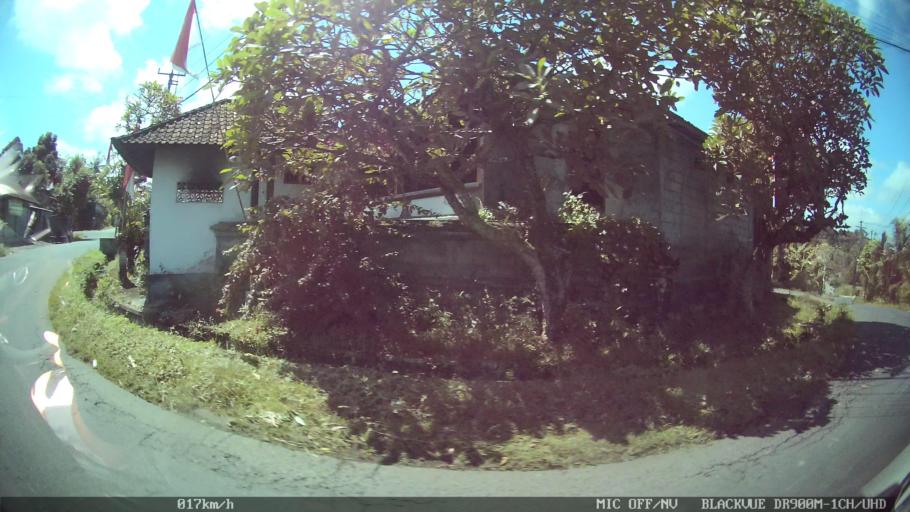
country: ID
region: Bali
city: Banjar Kelodan
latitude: -8.5268
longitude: 115.3352
